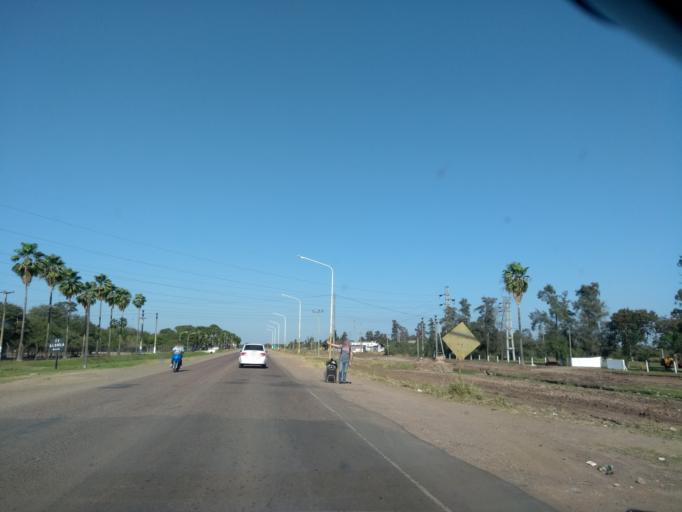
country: AR
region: Chaco
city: Presidencia Roque Saenz Pena
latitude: -26.8148
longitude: -60.4194
